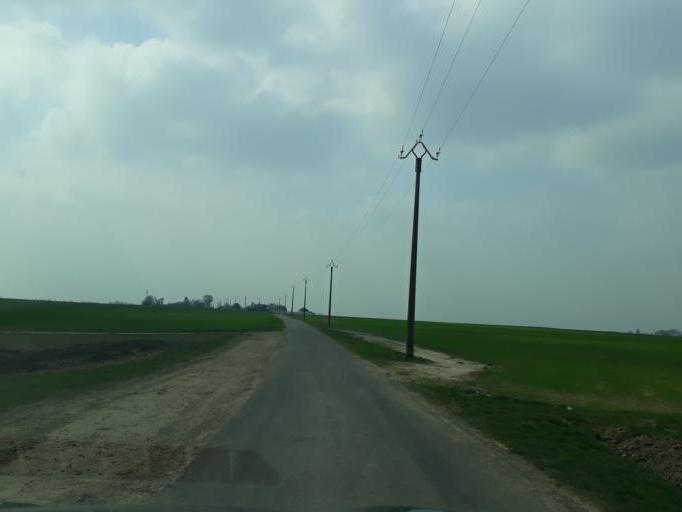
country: FR
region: Centre
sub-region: Departement d'Eure-et-Loir
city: Baigneaux
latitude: 48.0737
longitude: 1.8025
